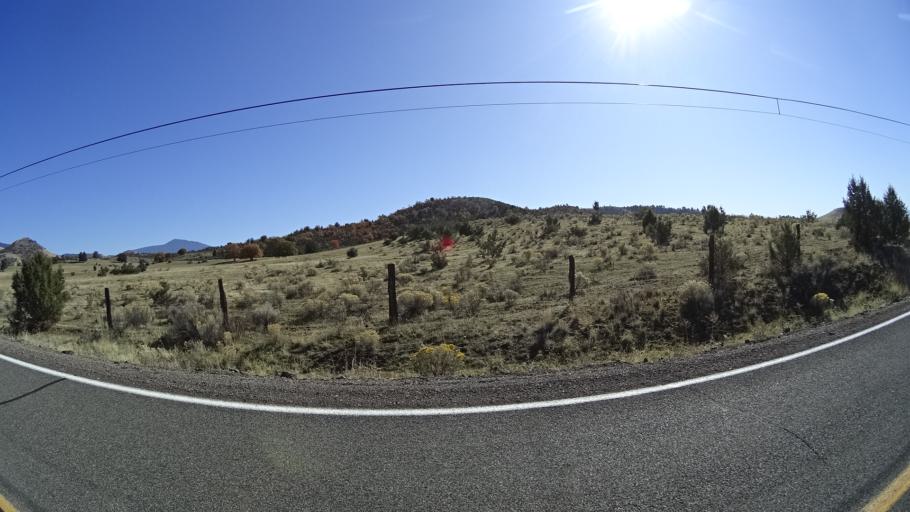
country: US
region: California
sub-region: Siskiyou County
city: Montague
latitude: 41.8045
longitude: -122.3948
